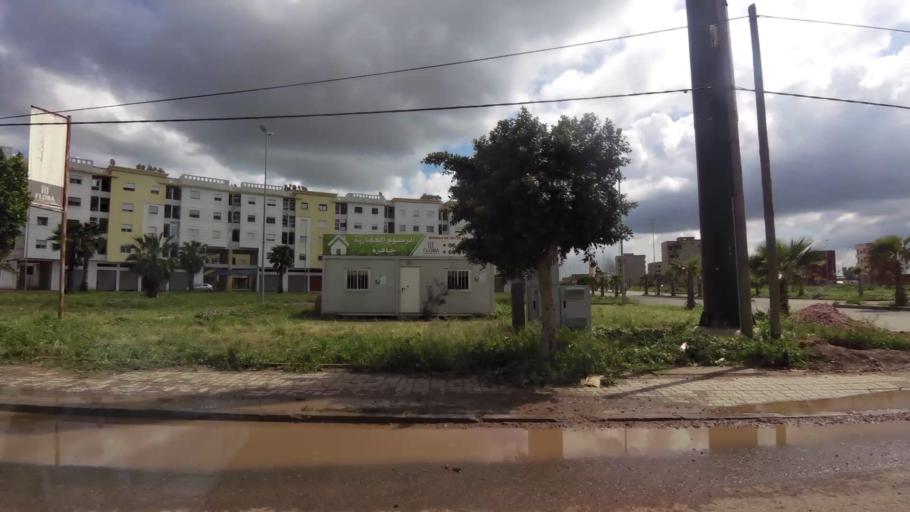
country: MA
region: Chaouia-Ouardigha
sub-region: Settat Province
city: Berrechid
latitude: 33.2632
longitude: -7.5977
